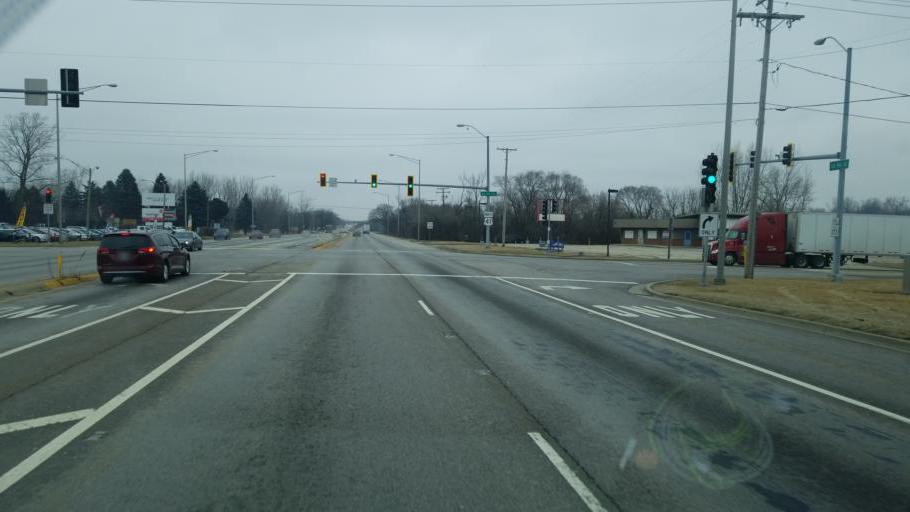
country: US
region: Illinois
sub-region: Lake County
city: Wadsworth
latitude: 42.4650
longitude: -87.9464
